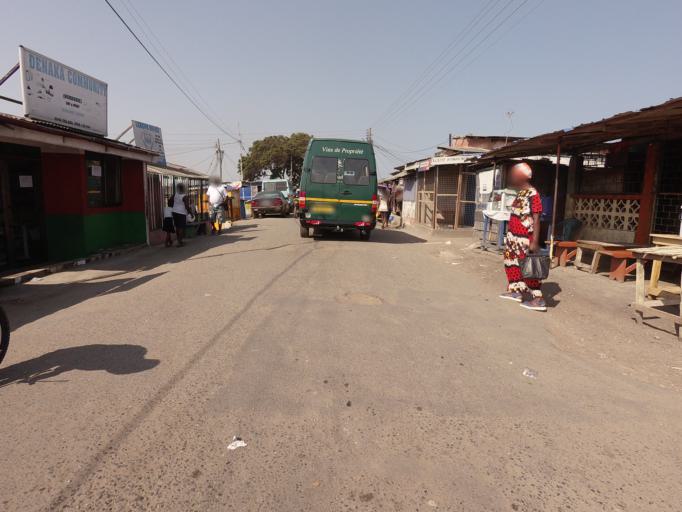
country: GH
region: Greater Accra
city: Teshi Old Town
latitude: 5.5791
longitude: -0.1037
